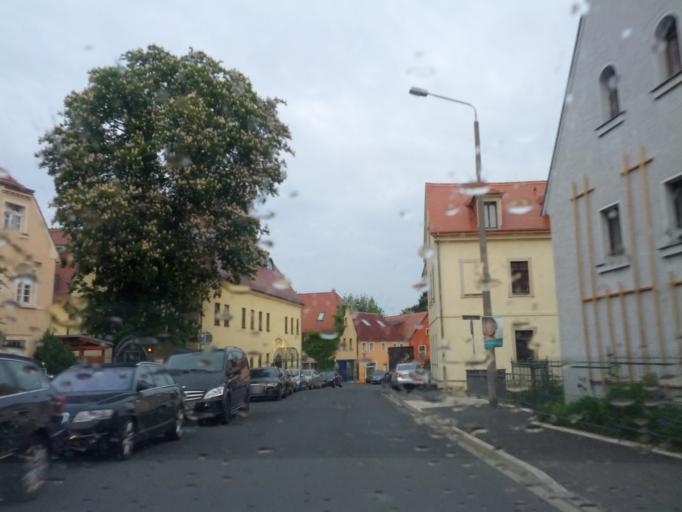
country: DE
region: Saxony
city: Dresden
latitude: 51.0140
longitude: 13.7663
